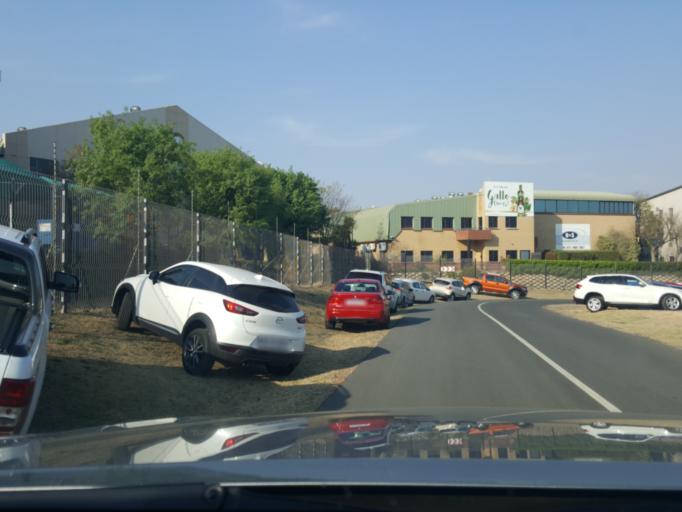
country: ZA
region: Gauteng
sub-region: City of Johannesburg Metropolitan Municipality
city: Midrand
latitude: -25.9927
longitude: 28.0728
